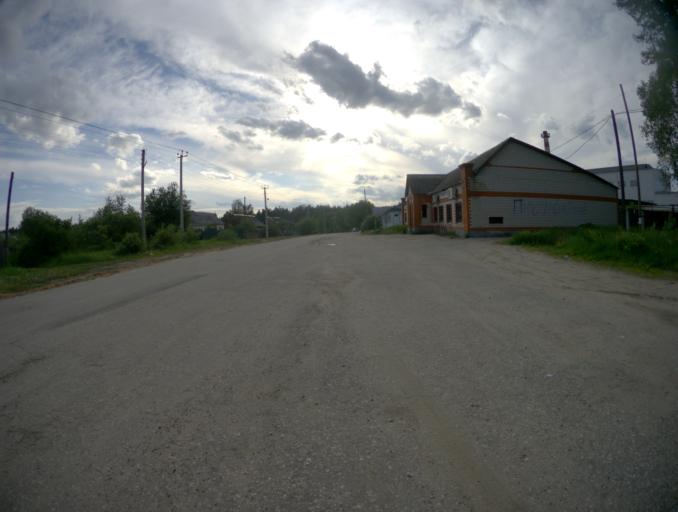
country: RU
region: Vladimir
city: Zolotkovo
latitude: 55.4050
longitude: 40.9084
